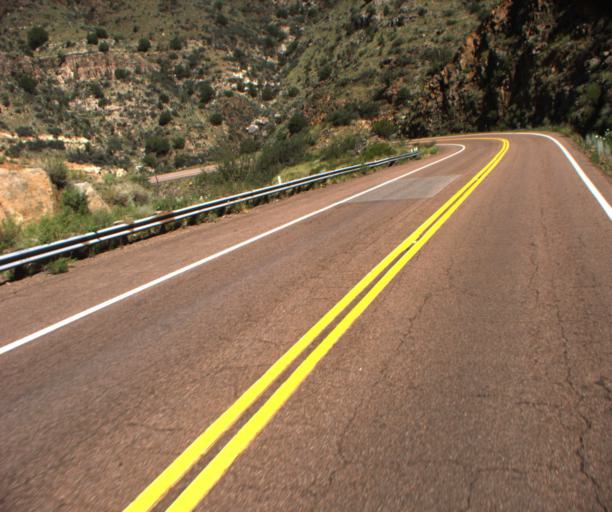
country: US
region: Arizona
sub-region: Navajo County
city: Cibecue
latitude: 33.8054
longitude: -110.4835
